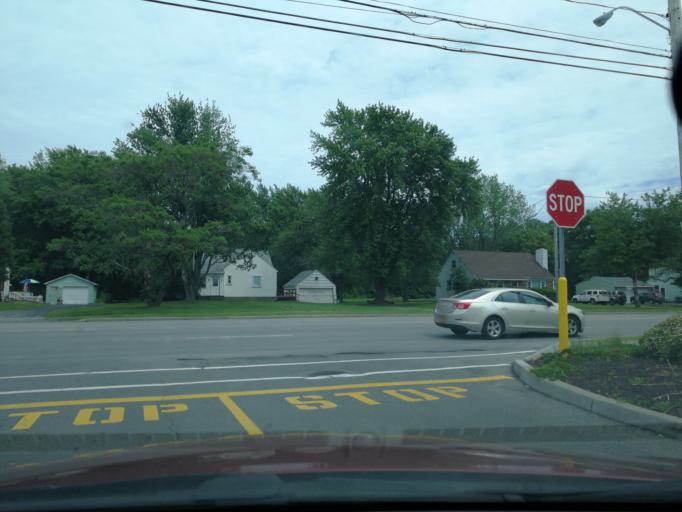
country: US
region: New York
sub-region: Monroe County
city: Greece
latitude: 43.2545
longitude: -77.6967
